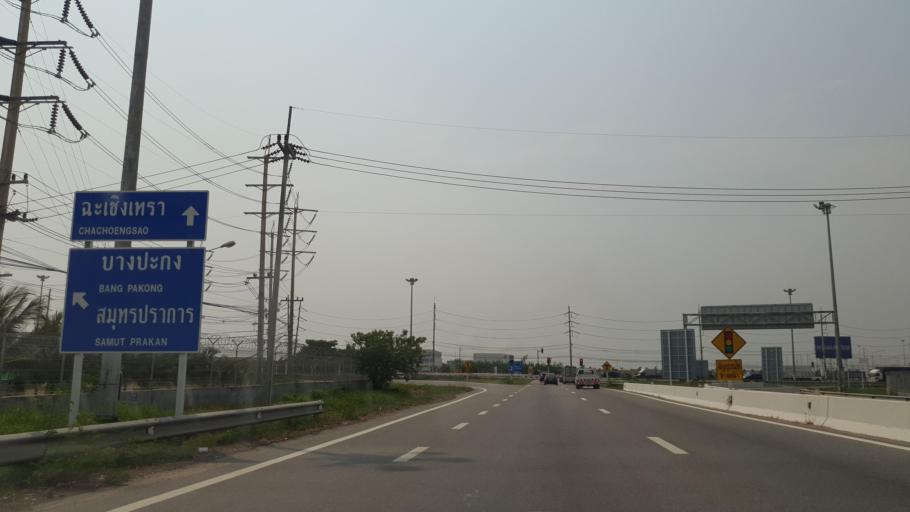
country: TH
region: Chachoengsao
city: Bang Pakong
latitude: 13.5546
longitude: 100.9935
